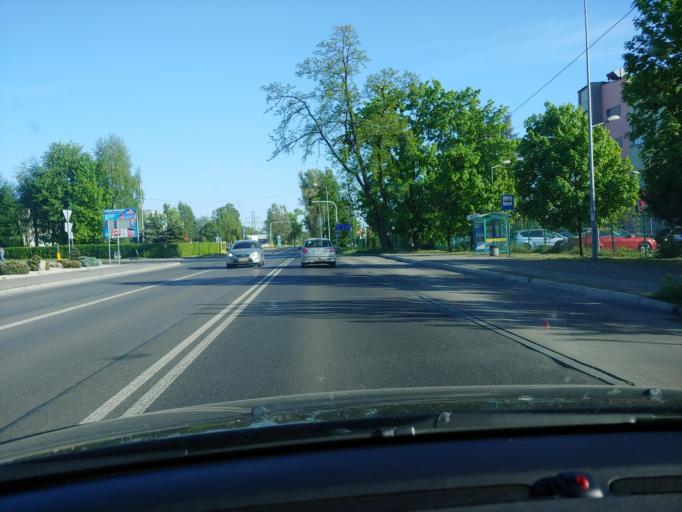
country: PL
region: Silesian Voivodeship
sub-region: Jaworzno
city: Jaworzno
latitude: 50.1932
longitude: 19.2838
